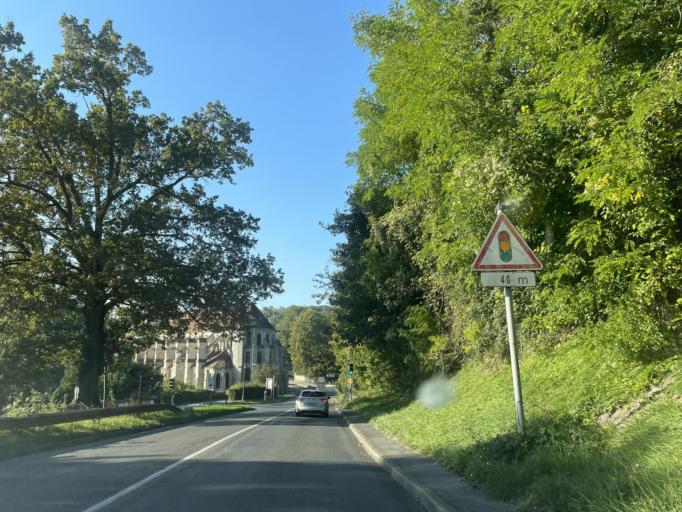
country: FR
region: Ile-de-France
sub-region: Departement de Seine-et-Marne
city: La Chapelle-sur-Crecy
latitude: 48.8572
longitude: 2.9277
